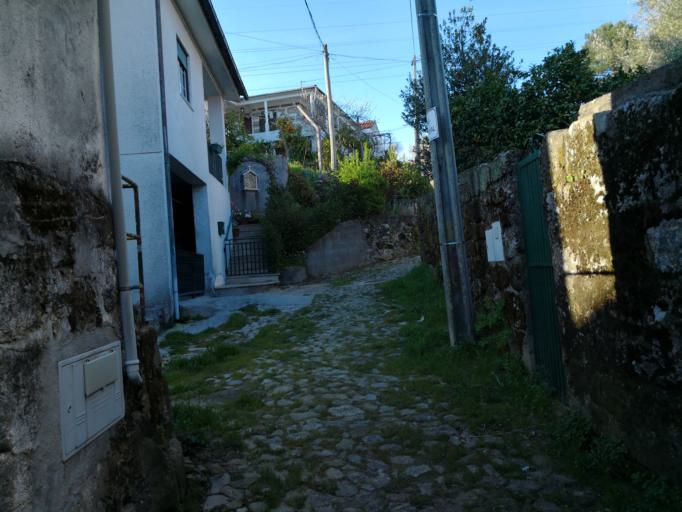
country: PT
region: Vila Real
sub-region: Vila Real
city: Vila Real
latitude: 41.2879
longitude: -7.7876
